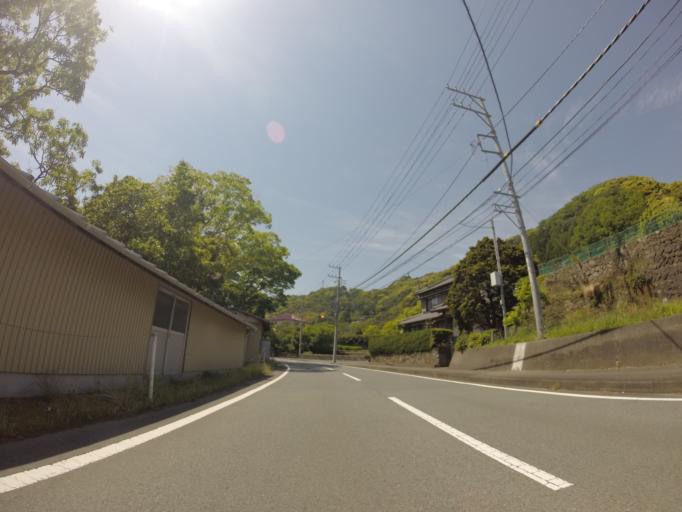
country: JP
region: Shizuoka
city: Shimoda
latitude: 34.7688
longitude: 138.9735
